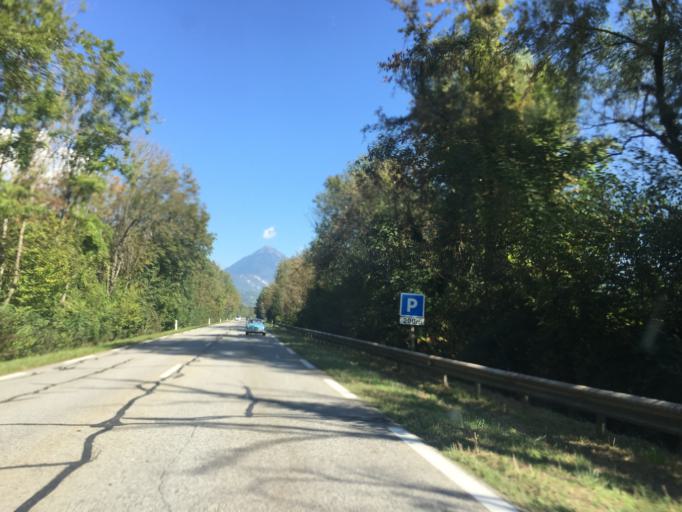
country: FR
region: Rhone-Alpes
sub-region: Departement de la Savoie
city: Gresy-sur-Isere
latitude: 45.5946
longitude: 6.2751
